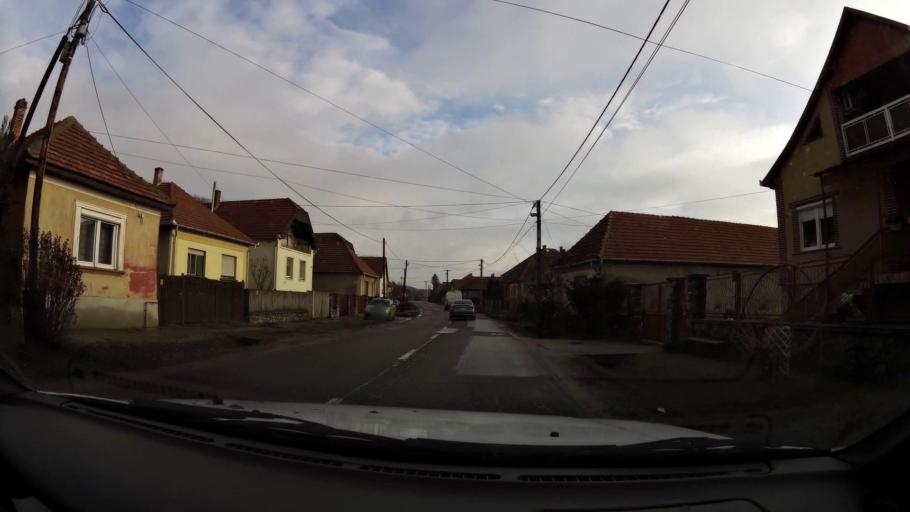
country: HU
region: Borsod-Abauj-Zemplen
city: Mucsony
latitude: 48.2679
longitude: 20.6852
